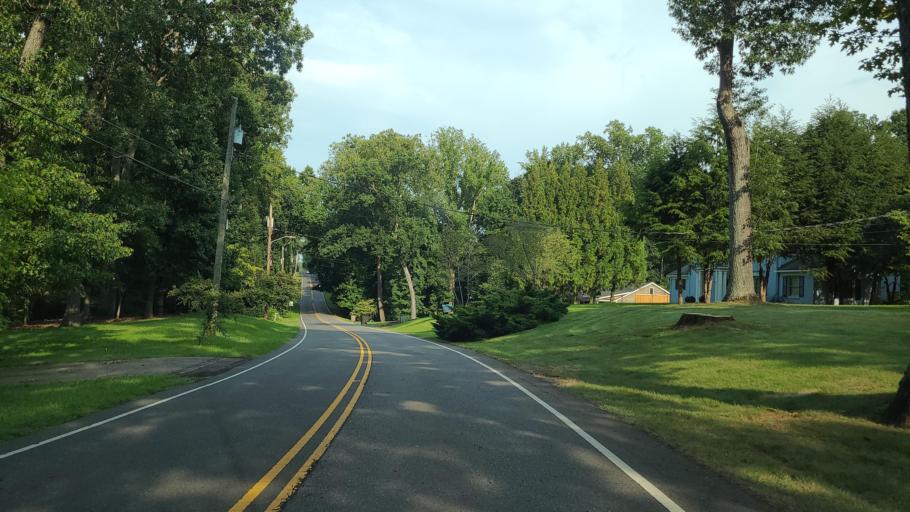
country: US
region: North Carolina
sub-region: Cleveland County
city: Shelby
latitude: 35.2928
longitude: -81.5628
